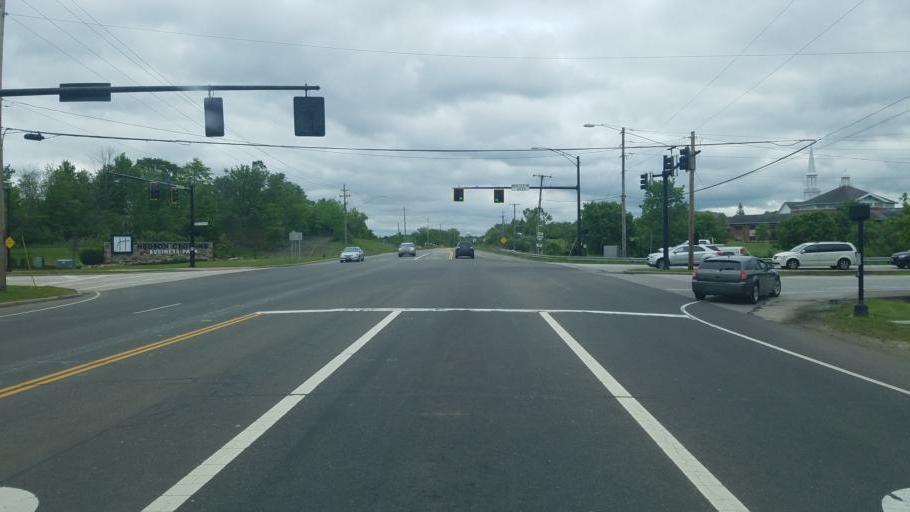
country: US
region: Ohio
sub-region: Summit County
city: Boston Heights
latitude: 41.2326
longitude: -81.4871
